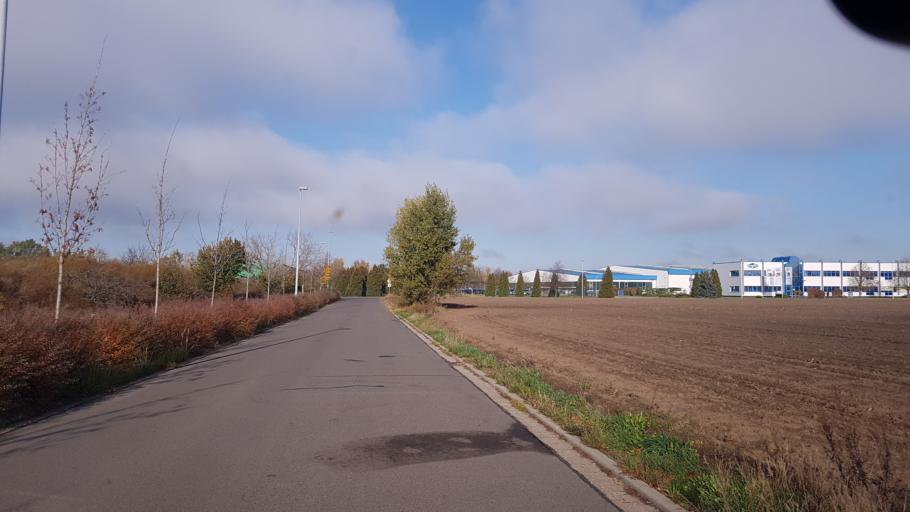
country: DE
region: Brandenburg
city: Elsterwerda
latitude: 51.4626
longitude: 13.5482
